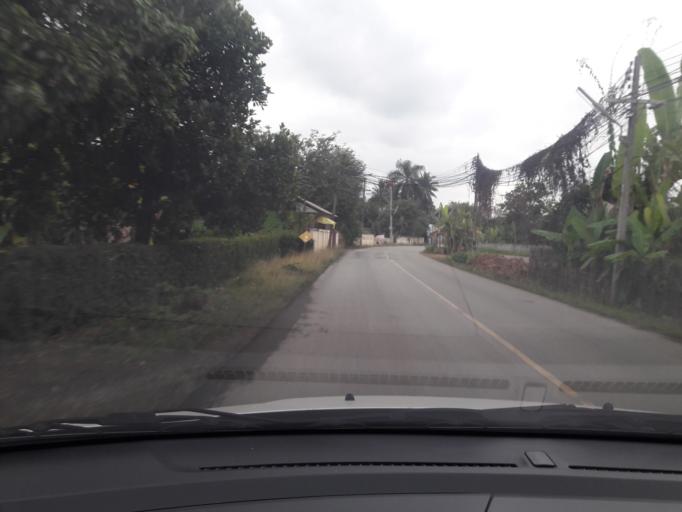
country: TH
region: Chiang Mai
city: Saraphi
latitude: 18.7155
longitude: 99.0502
